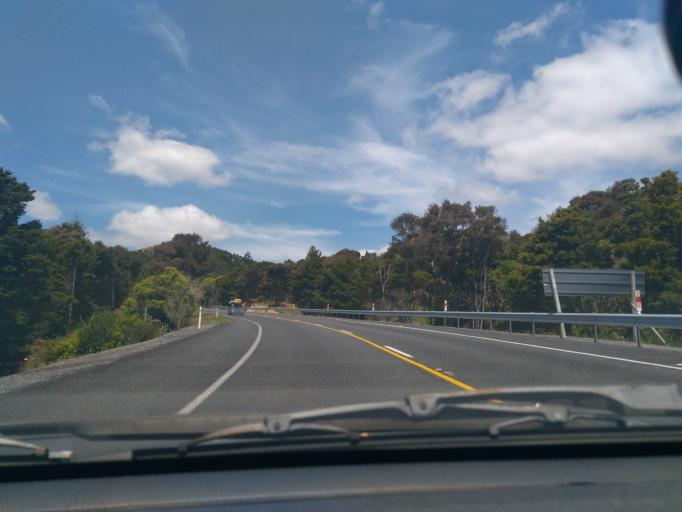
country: NZ
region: Northland
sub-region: Far North District
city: Kerikeri
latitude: -35.1175
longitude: 173.8172
